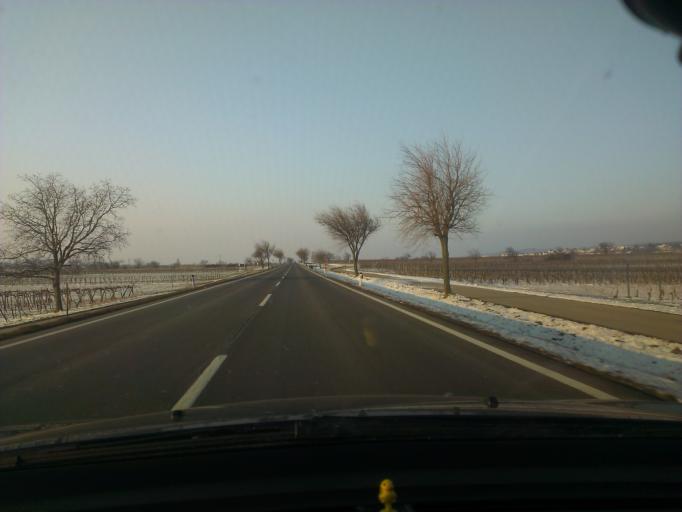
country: AT
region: Burgenland
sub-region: Eisenstadt-Umgebung
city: Breitenbrunn
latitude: 47.9276
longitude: 16.7135
